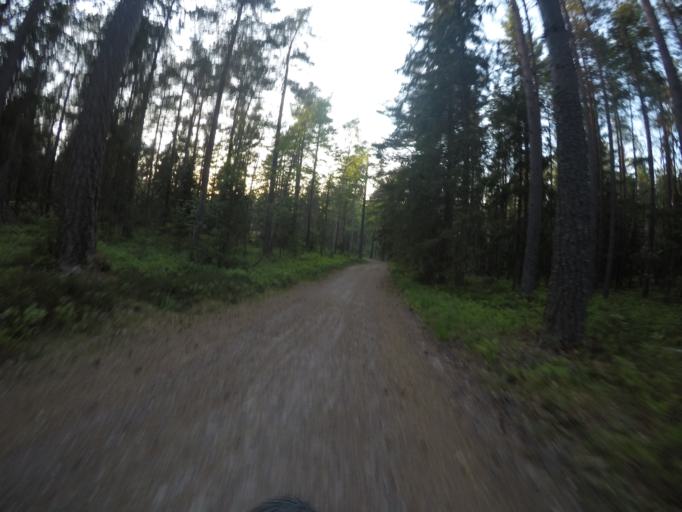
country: SE
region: Soedermanland
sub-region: Eskilstuna Kommun
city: Eskilstuna
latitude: 59.3427
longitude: 16.5124
